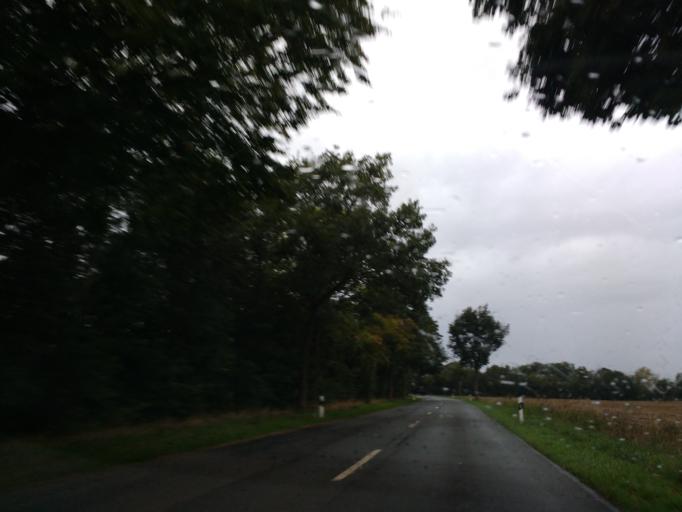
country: DE
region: North Rhine-Westphalia
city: Rietberg
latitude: 51.7281
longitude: 8.4377
